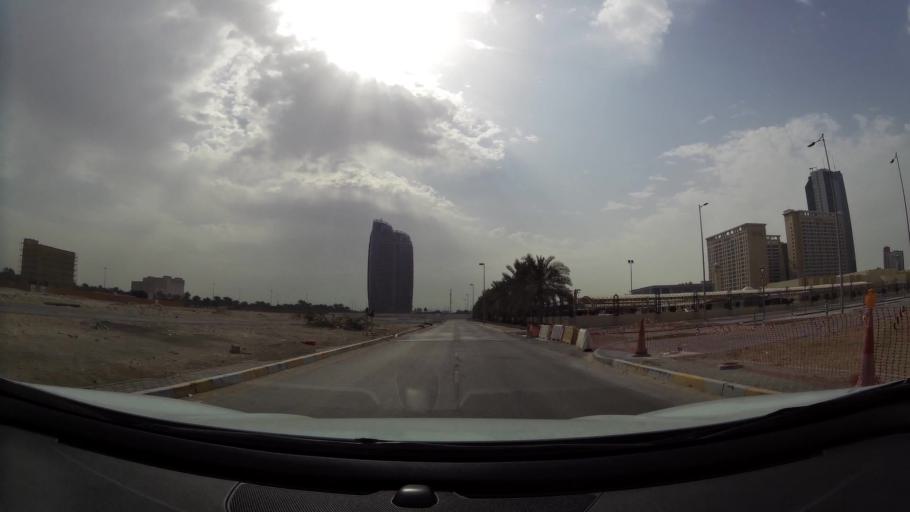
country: AE
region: Abu Dhabi
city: Abu Dhabi
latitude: 24.4601
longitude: 54.3956
